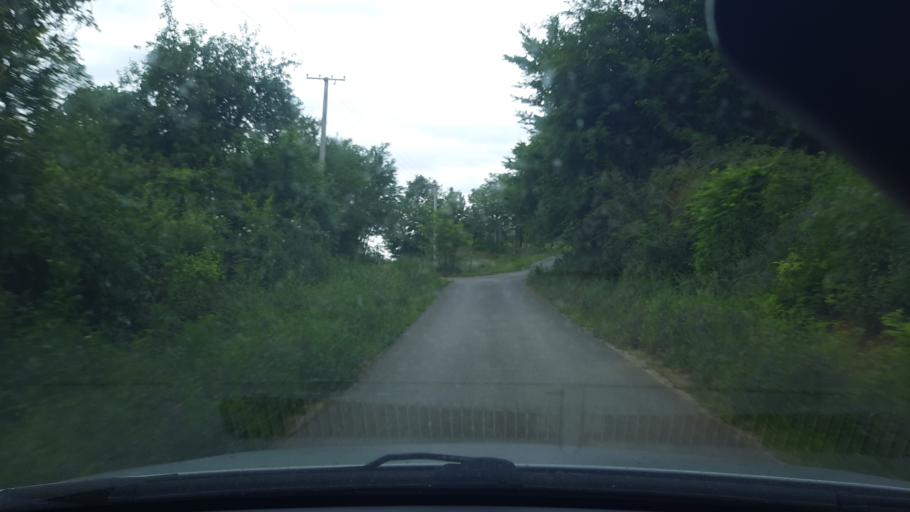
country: RS
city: Jarebice
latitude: 44.4933
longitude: 19.4791
